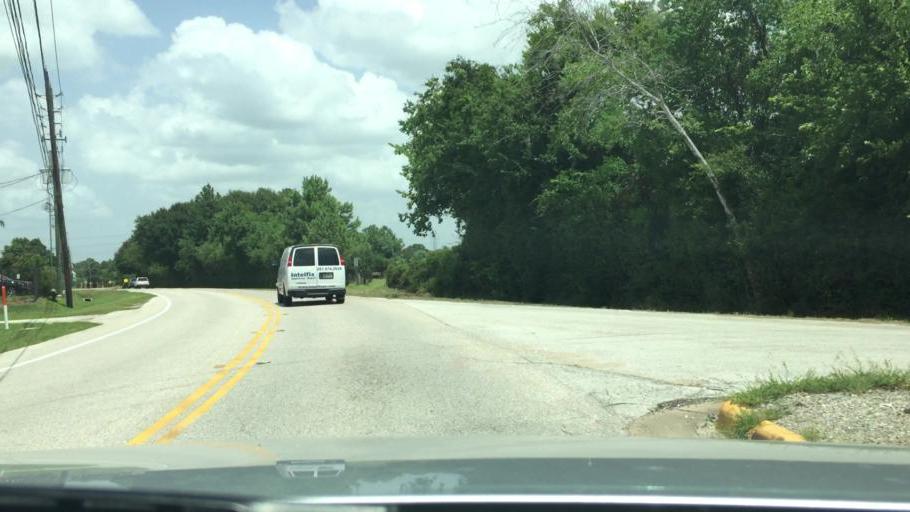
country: US
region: Texas
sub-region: Harris County
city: Hudson
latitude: 29.9402
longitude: -95.5163
